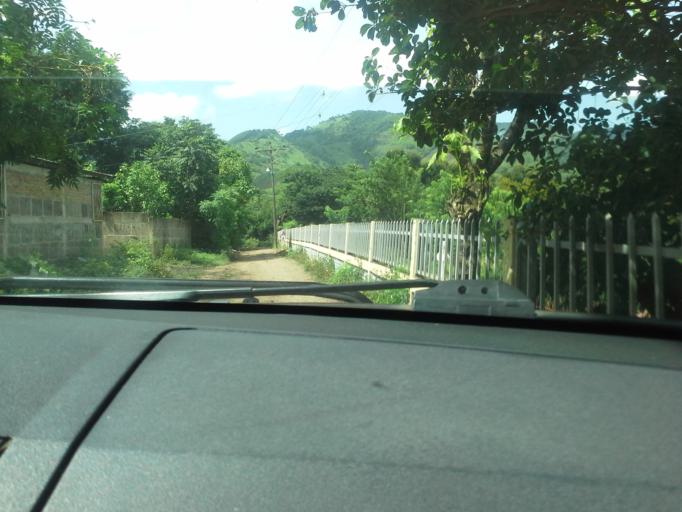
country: NI
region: Matagalpa
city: Terrabona
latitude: 12.7266
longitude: -85.9650
